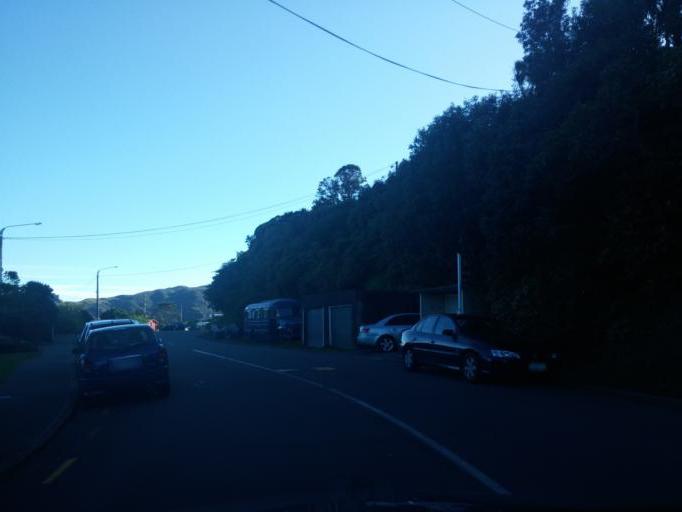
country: NZ
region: Wellington
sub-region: Wellington City
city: Kelburn
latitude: -41.2765
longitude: 174.7595
